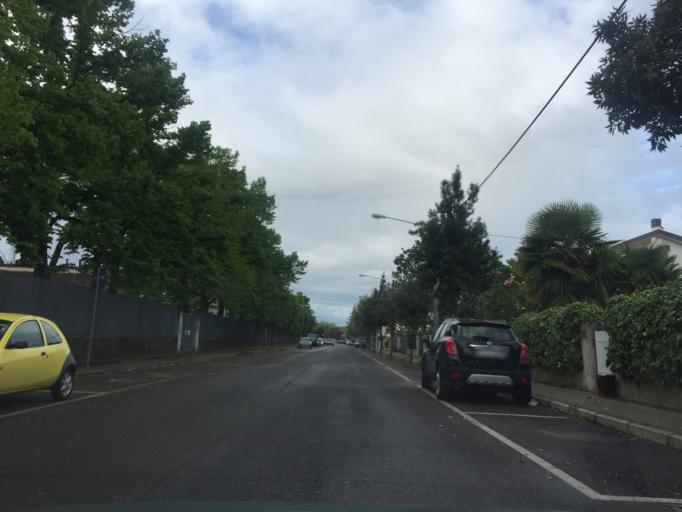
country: IT
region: Friuli Venezia Giulia
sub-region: Provincia di Gorizia
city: Gorizia
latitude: 45.9323
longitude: 13.6027
